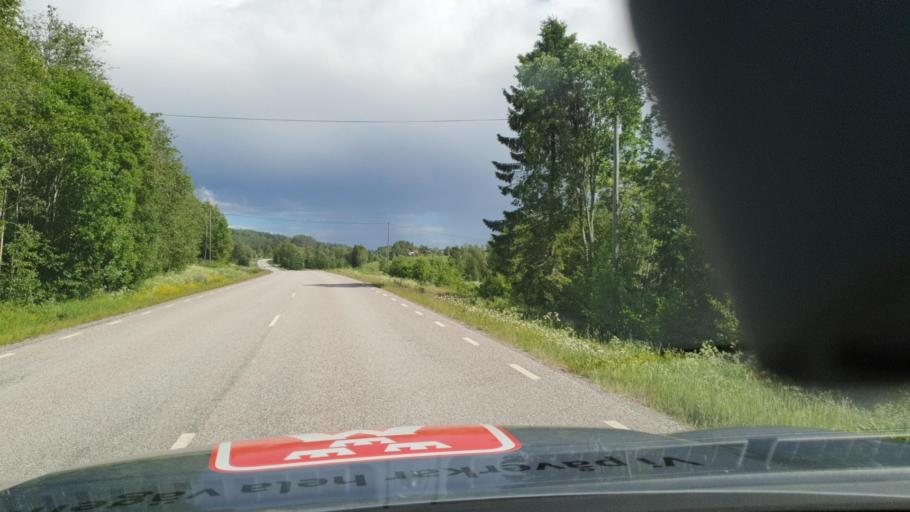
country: SE
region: Vaesternorrland
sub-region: OErnskoeldsviks Kommun
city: Bjasta
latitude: 63.2593
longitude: 18.3458
